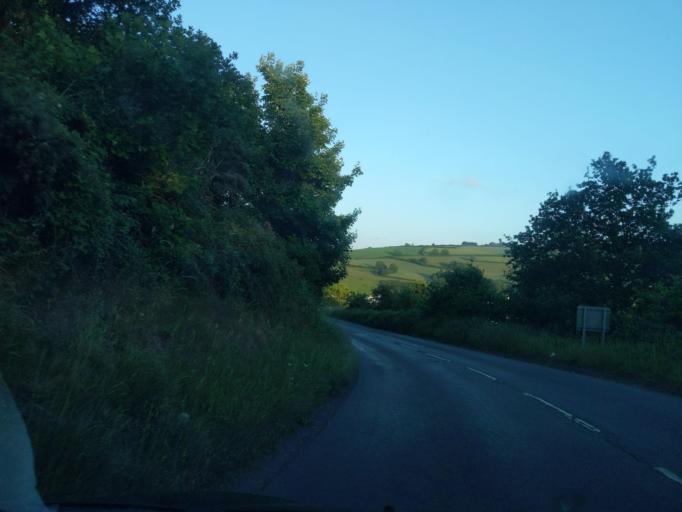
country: GB
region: England
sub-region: Devon
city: Great Torrington
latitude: 50.9521
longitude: -4.1580
